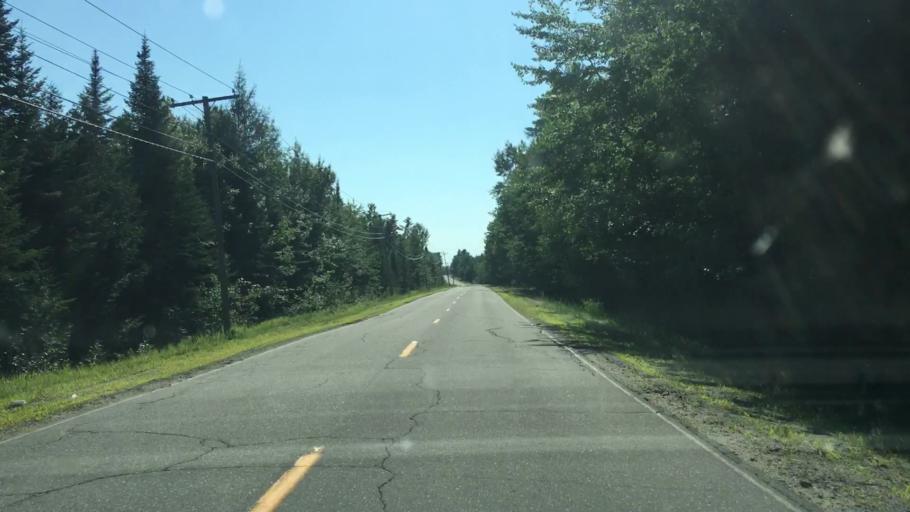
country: US
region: Maine
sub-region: Penobscot County
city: Enfield
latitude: 45.2450
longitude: -68.6084
